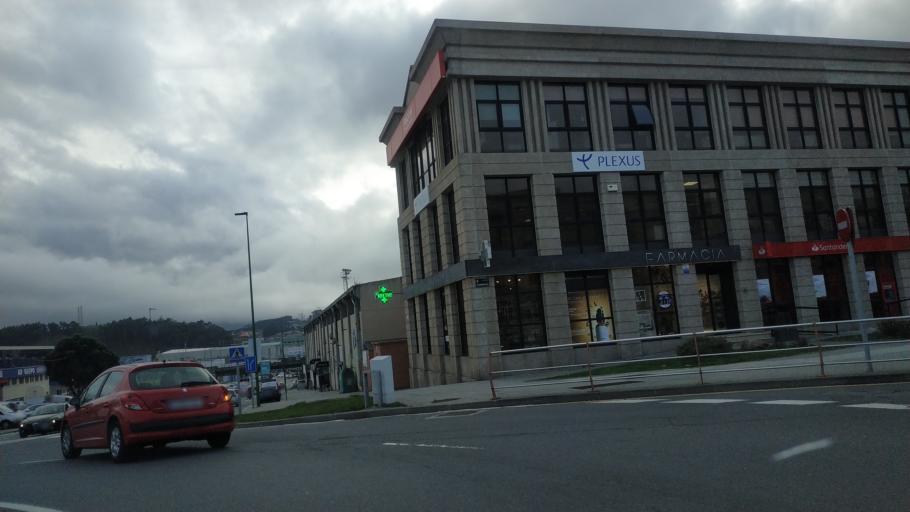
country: ES
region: Galicia
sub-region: Provincia da Coruna
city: A Coruna
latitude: 43.3525
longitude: -8.4225
